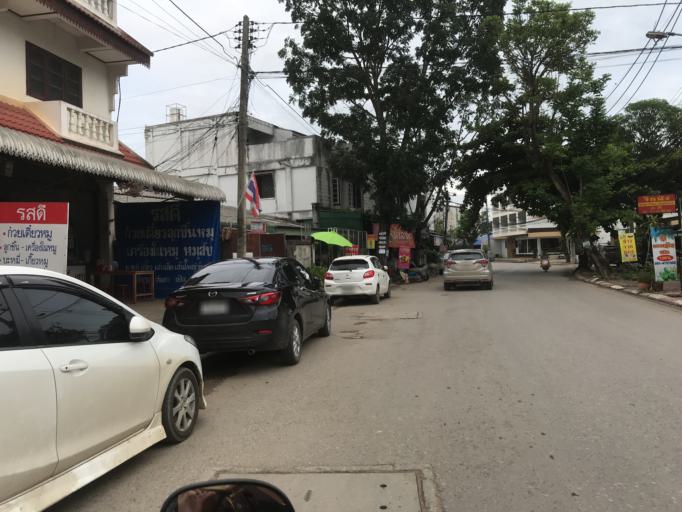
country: TH
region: Chiang Rai
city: Chiang Rai
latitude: 19.8991
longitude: 99.8298
